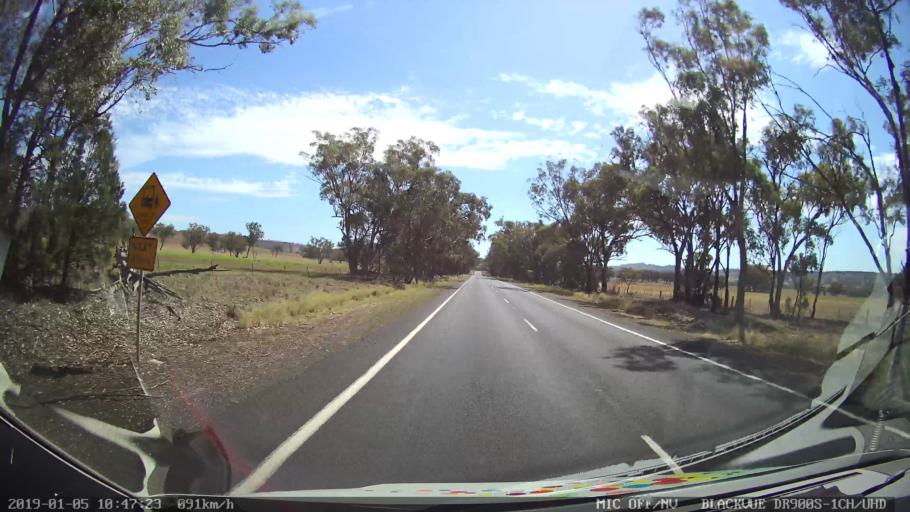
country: AU
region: New South Wales
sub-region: Warrumbungle Shire
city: Coonabarabran
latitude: -31.4454
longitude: 149.0322
